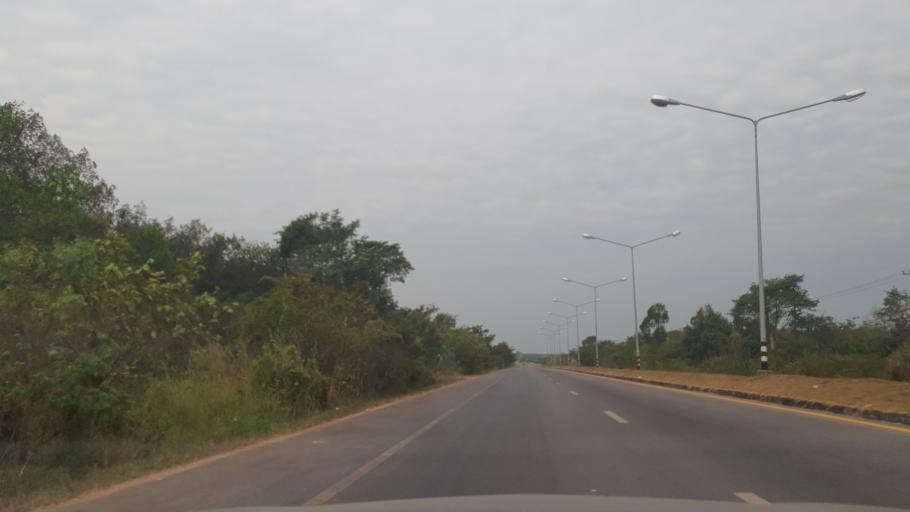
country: TH
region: Changwat Bueng Kan
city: Bung Khla
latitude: 18.2964
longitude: 103.9804
